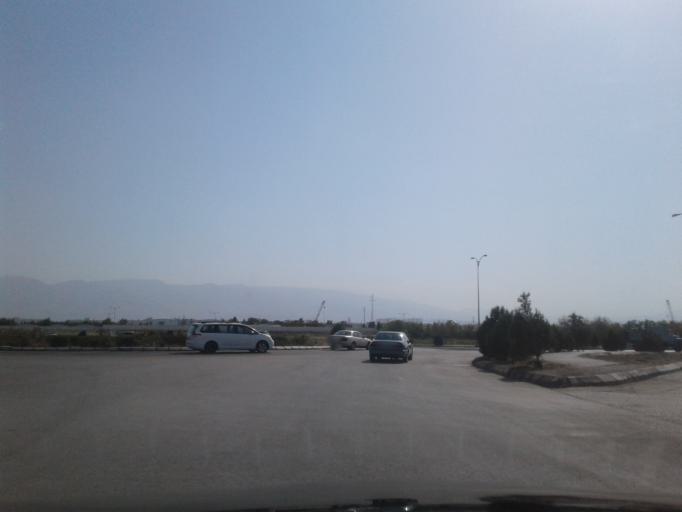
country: TM
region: Ahal
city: Ashgabat
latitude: 37.9701
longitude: 58.4230
